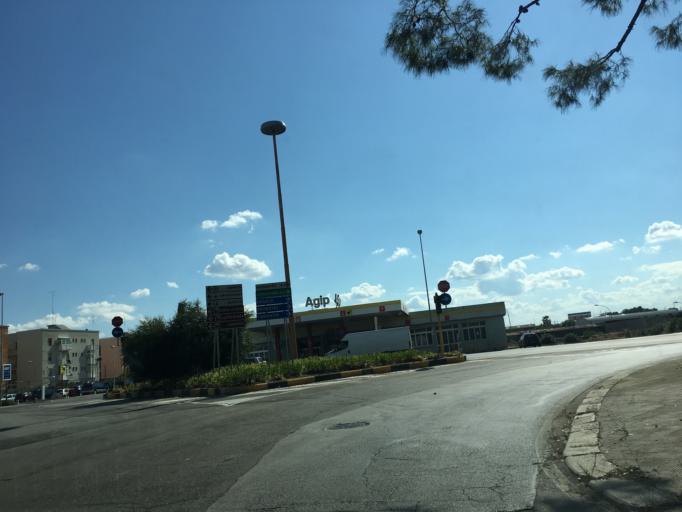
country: IT
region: Apulia
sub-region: Provincia di Bari
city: Bari
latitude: 41.1308
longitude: 16.8315
